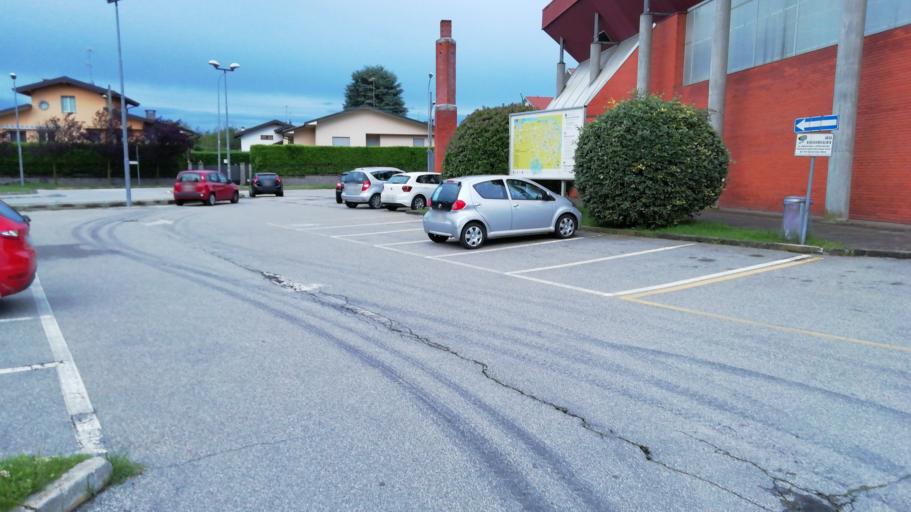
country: IT
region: Piedmont
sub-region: Provincia di Novara
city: Castelletto Sopra Ticino
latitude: 45.7097
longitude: 8.6334
